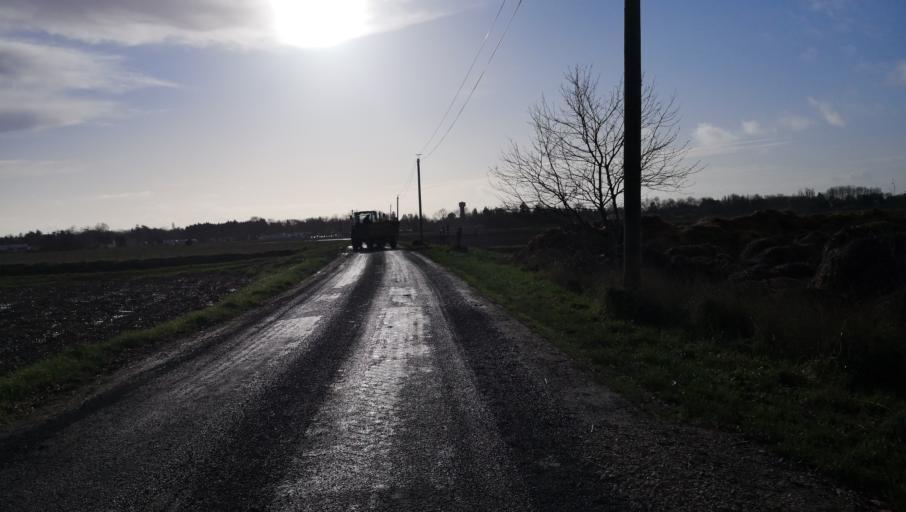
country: FR
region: Centre
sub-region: Departement du Loiret
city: La Chapelle-Saint-Mesmin
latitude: 47.8815
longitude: 1.8460
